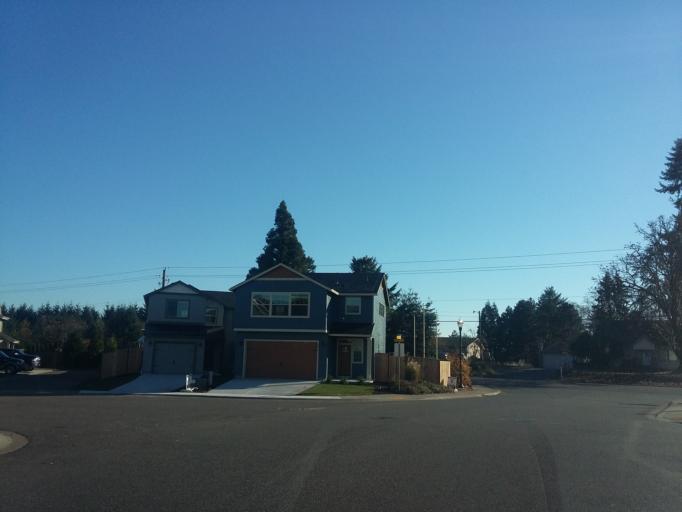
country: US
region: Washington
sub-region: Clark County
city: Barberton
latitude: 45.6888
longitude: -122.6230
